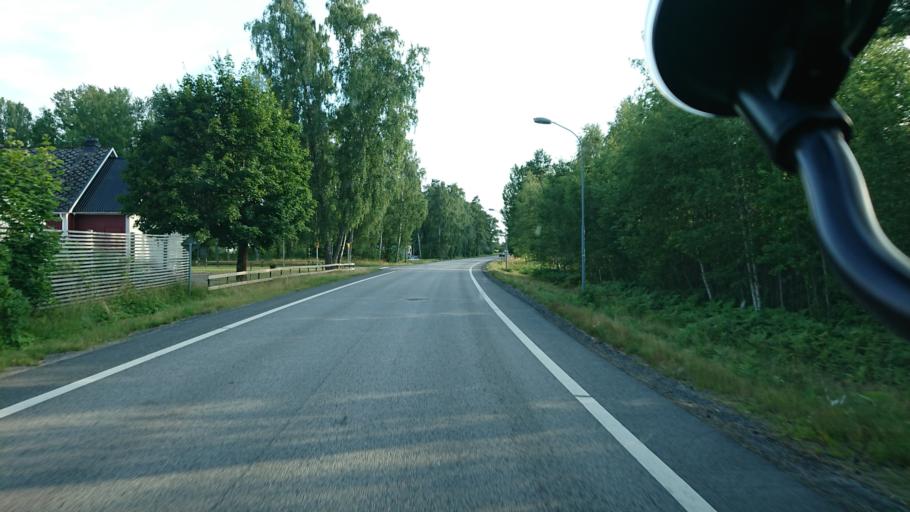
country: SE
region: Kronoberg
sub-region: Vaxjo Kommun
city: Rottne
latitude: 57.0302
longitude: 14.8952
